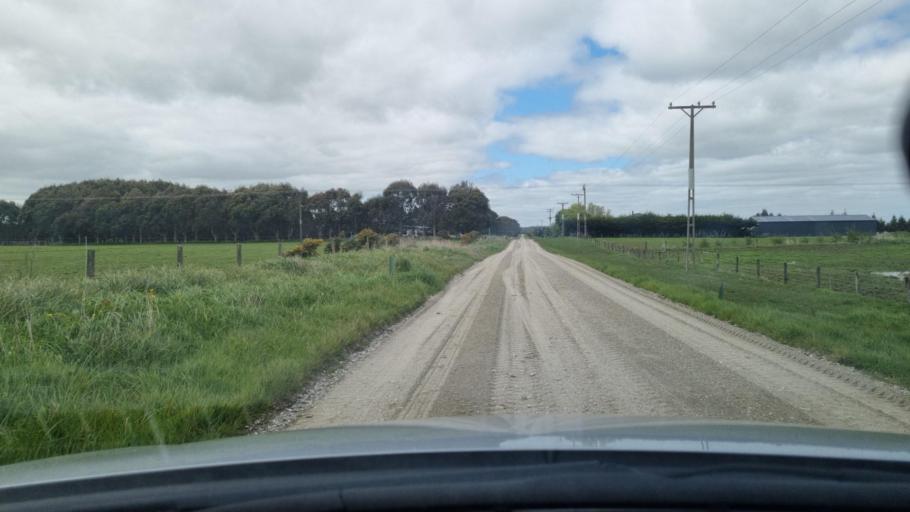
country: NZ
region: Southland
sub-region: Invercargill City
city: Invercargill
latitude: -46.4342
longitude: 168.4001
